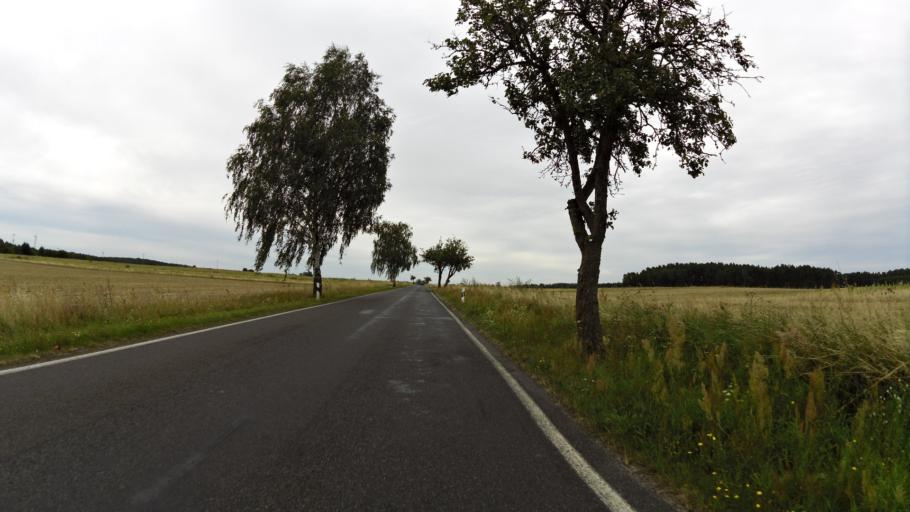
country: DE
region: Brandenburg
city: Wendisch Rietz
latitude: 52.1932
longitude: 14.0358
